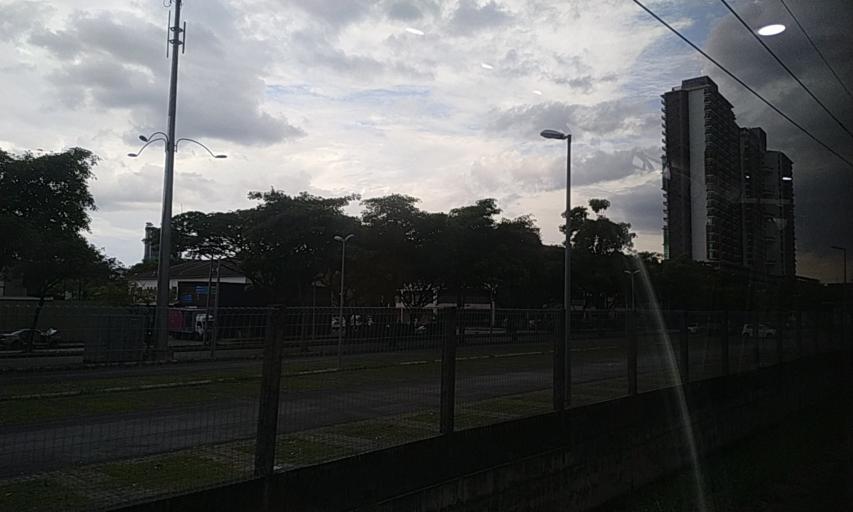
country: MY
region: Kuala Lumpur
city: Kuala Lumpur
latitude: 3.2158
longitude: 101.6723
